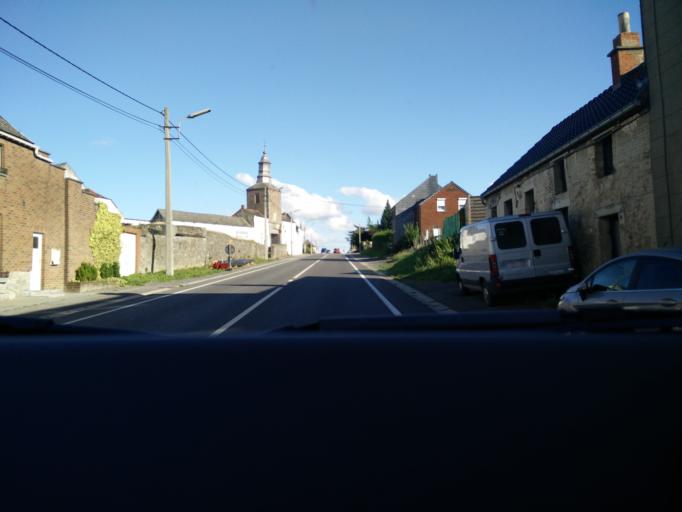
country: BE
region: Wallonia
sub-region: Province du Hainaut
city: Merbes-le-Chateau
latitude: 50.3063
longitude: 4.1456
